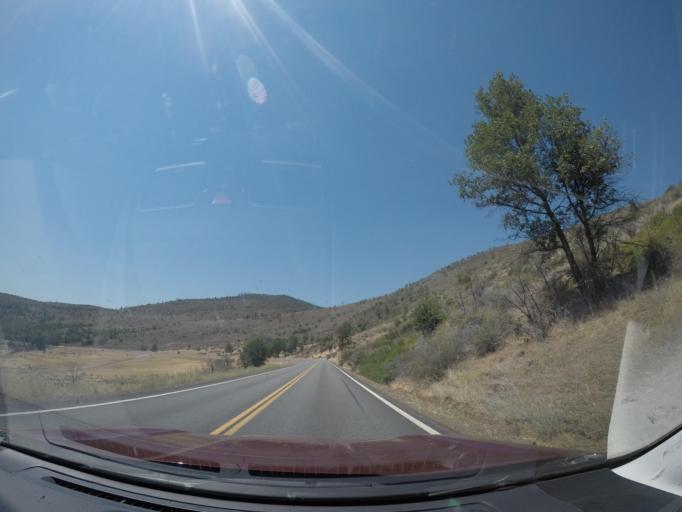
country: US
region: California
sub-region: Shasta County
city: Burney
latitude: 41.0005
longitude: -121.5014
